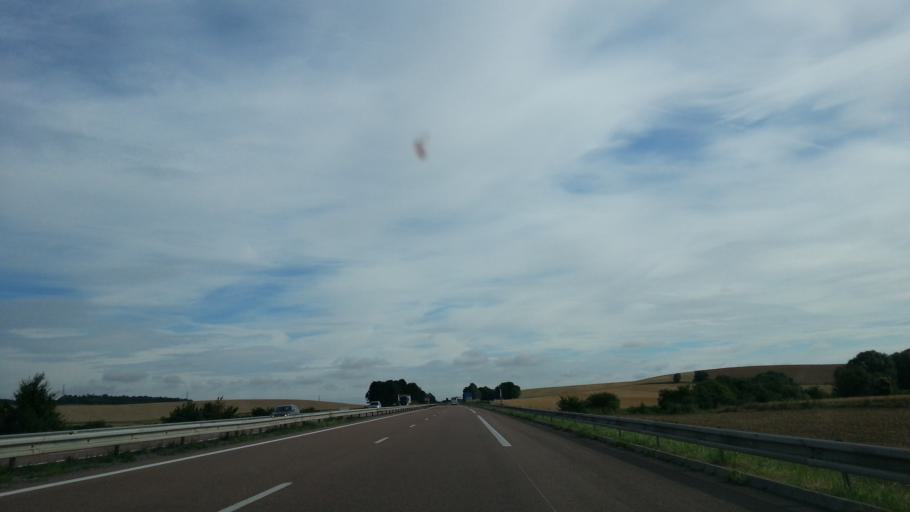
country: FR
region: Champagne-Ardenne
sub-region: Departement de la Marne
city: Chatillon-sur-Marne
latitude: 49.1806
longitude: 3.7495
